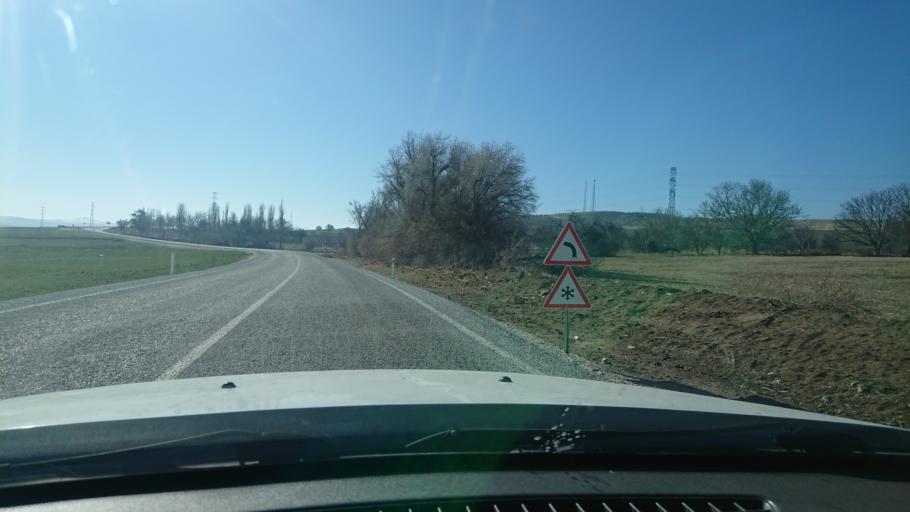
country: TR
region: Aksaray
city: Agacoren
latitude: 38.8890
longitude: 33.9279
